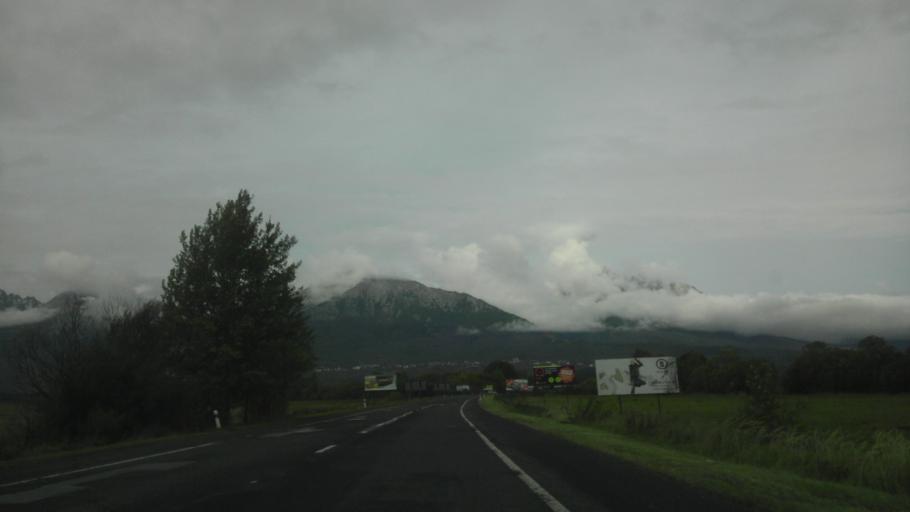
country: SK
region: Presovsky
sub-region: Okres Poprad
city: Nova Lesna
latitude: 49.0863
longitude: 20.2643
